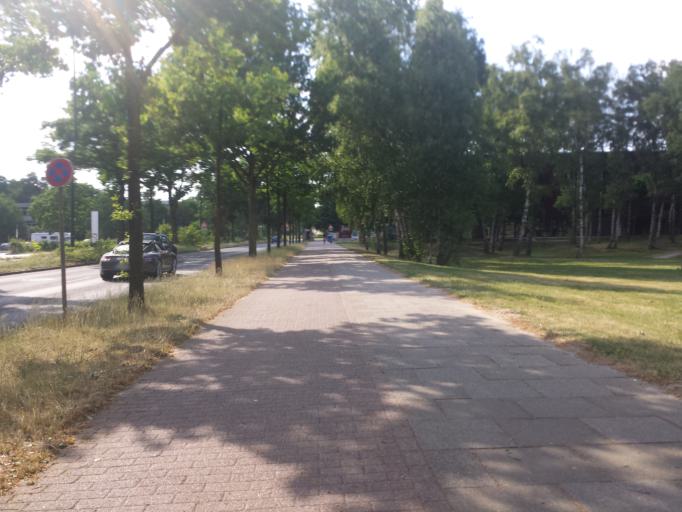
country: DE
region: Bremen
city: Bremen
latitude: 53.1056
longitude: 8.8495
